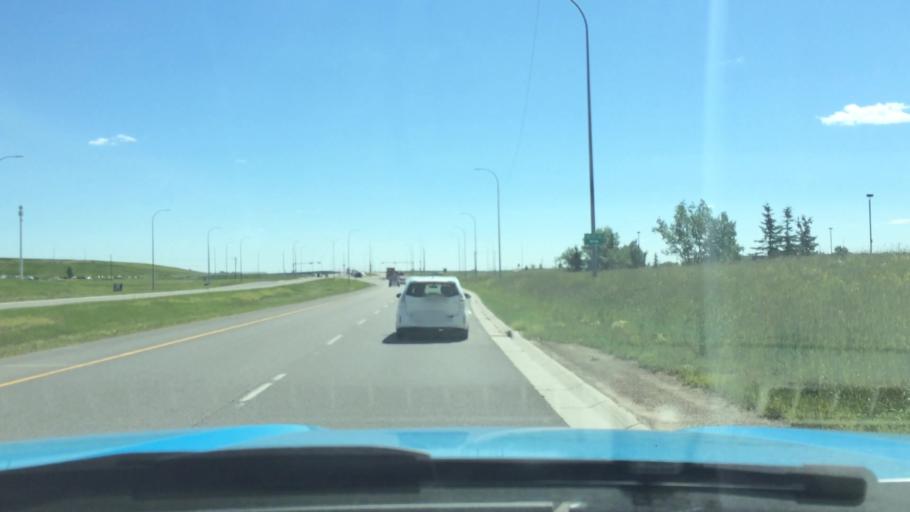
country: CA
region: Alberta
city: Calgary
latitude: 51.0147
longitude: -113.9637
